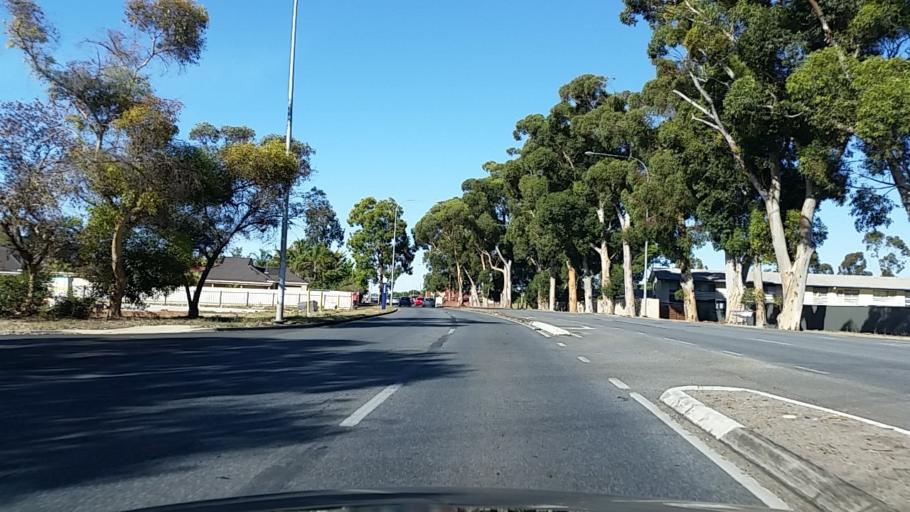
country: AU
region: South Australia
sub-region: Salisbury
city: Salisbury
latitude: -34.7580
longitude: 138.6449
